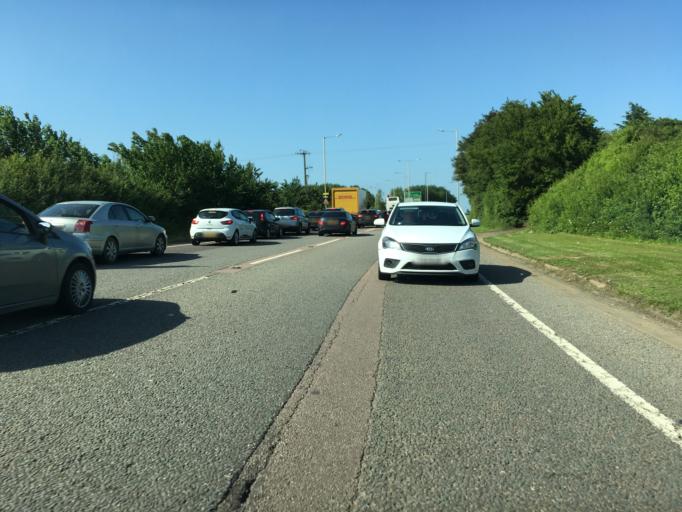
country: GB
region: England
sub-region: Milton Keynes
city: Water Eaton
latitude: 51.9905
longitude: -0.7010
